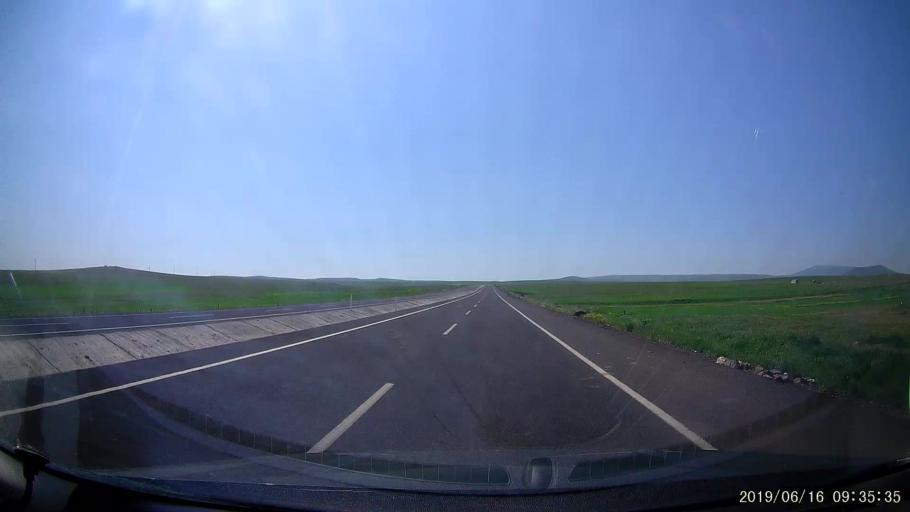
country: TR
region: Kars
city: Kars
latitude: 40.5698
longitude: 43.1581
